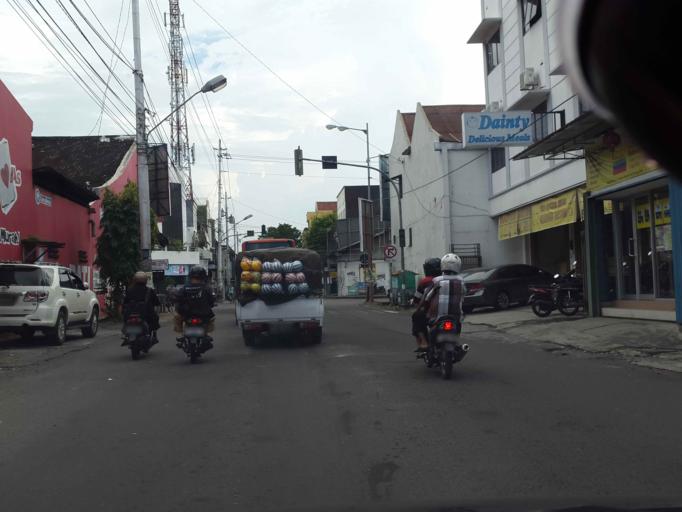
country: ID
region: Central Java
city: Surakarta
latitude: -7.5696
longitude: 110.8333
